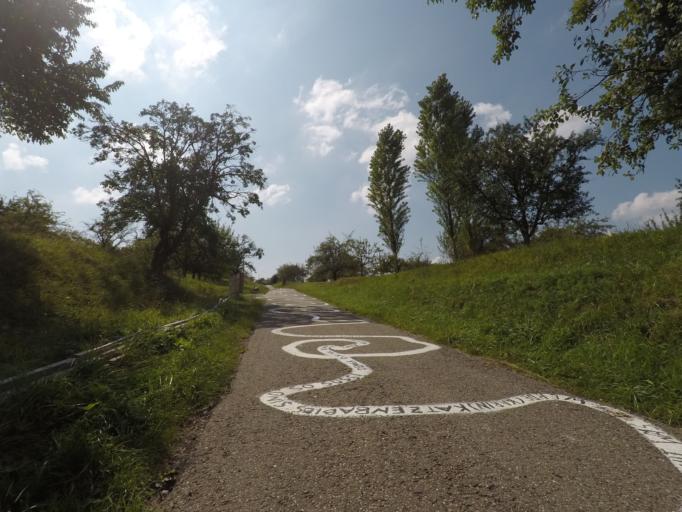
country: DE
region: Baden-Wuerttemberg
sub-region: Regierungsbezirk Stuttgart
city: Winterbach
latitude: 48.7952
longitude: 9.4726
